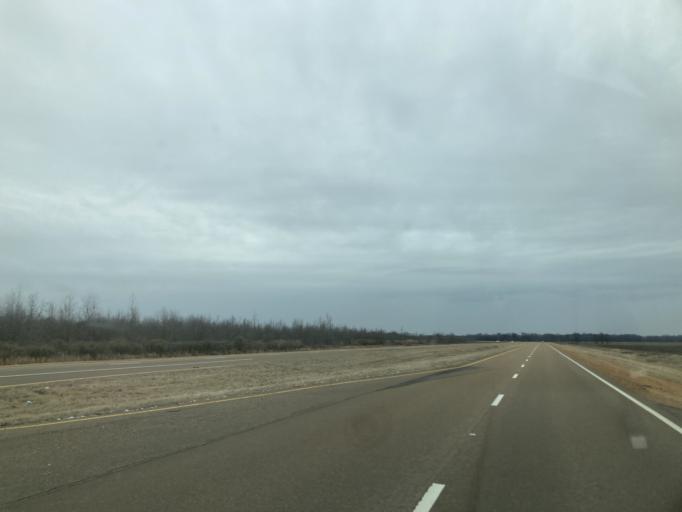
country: US
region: Mississippi
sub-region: Humphreys County
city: Belzoni
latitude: 33.0625
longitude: -90.4713
